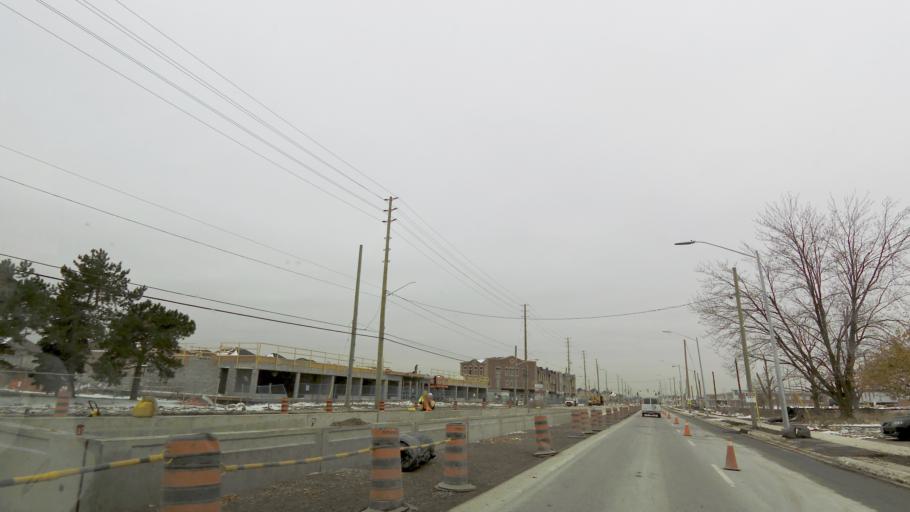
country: CA
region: Ontario
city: Vaughan
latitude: 43.8444
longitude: -79.5635
